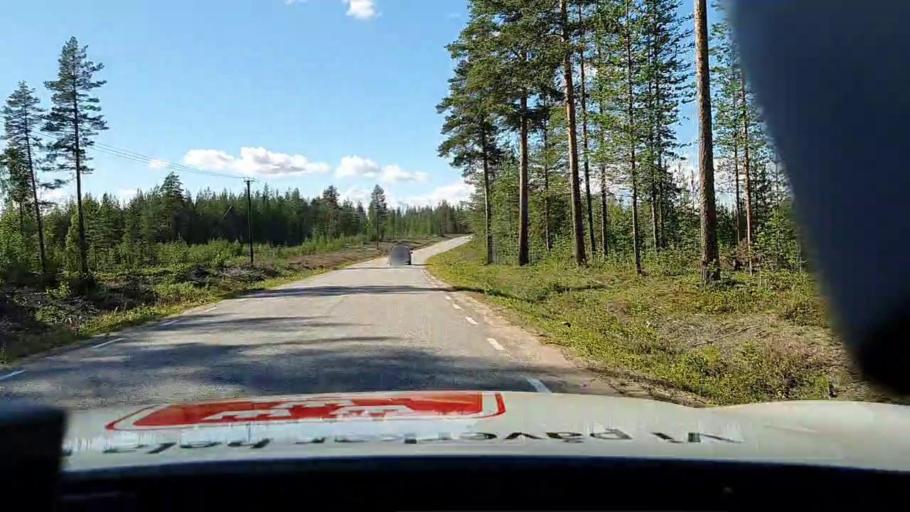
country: SE
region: Norrbotten
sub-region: Overkalix Kommun
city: OEverkalix
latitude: 66.2364
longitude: 22.9365
